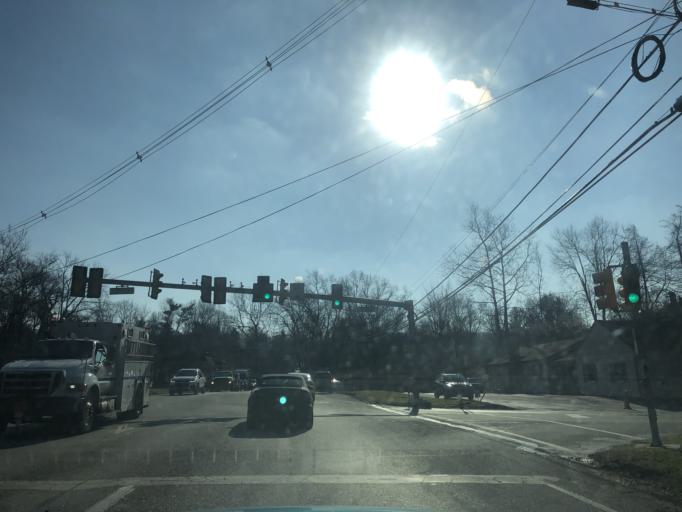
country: US
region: Pennsylvania
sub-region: Delaware County
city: Radnor
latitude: 40.0620
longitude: -75.3410
